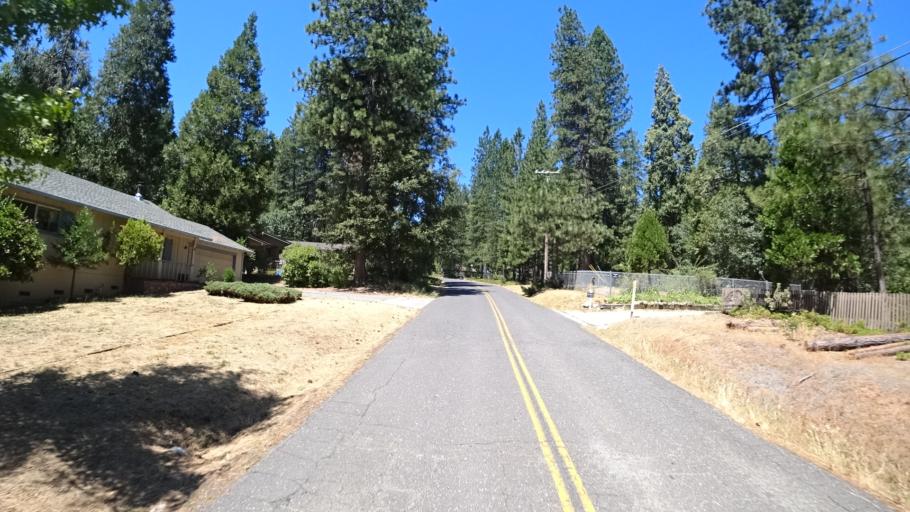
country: US
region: California
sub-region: Calaveras County
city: Forest Meadows
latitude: 38.2060
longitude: -120.3759
